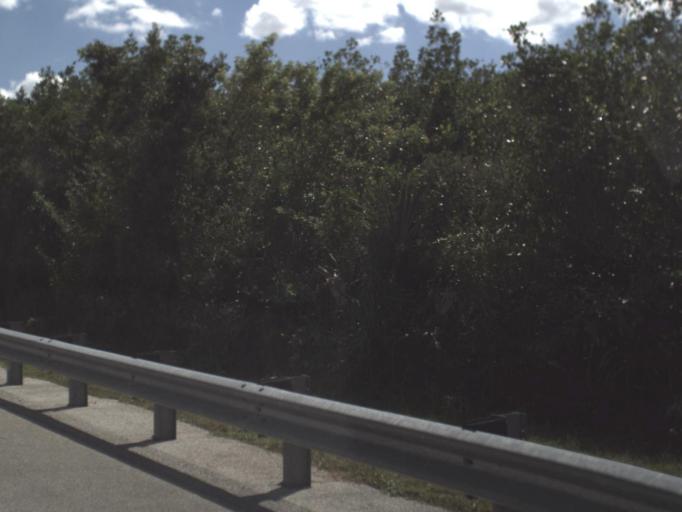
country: US
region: Florida
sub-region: Collier County
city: Marco
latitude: 25.9811
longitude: -81.5623
